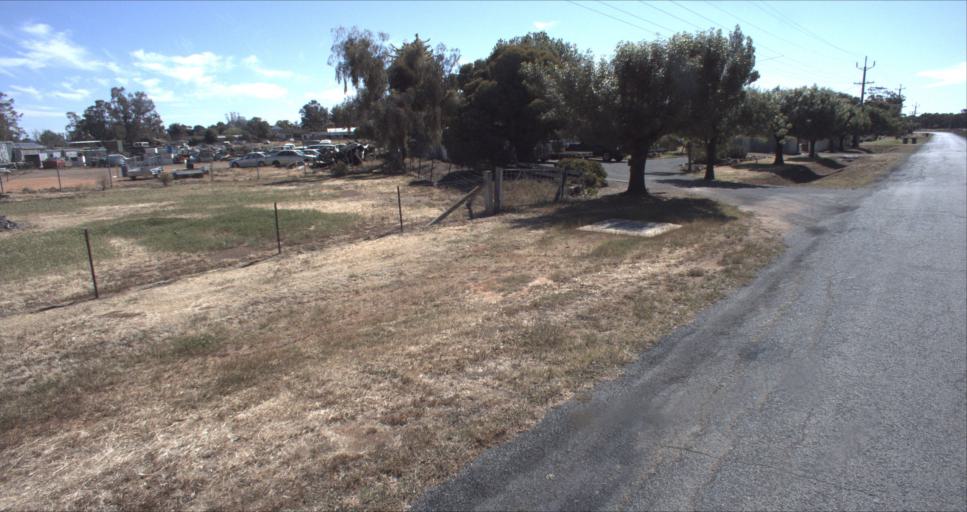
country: AU
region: New South Wales
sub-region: Leeton
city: Leeton
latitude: -34.5503
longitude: 146.3822
